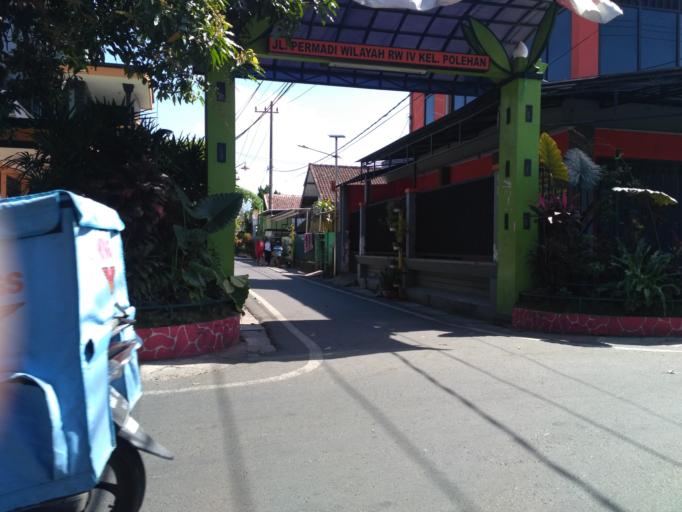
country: ID
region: East Java
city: Malang
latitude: -7.9884
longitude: 112.6449
